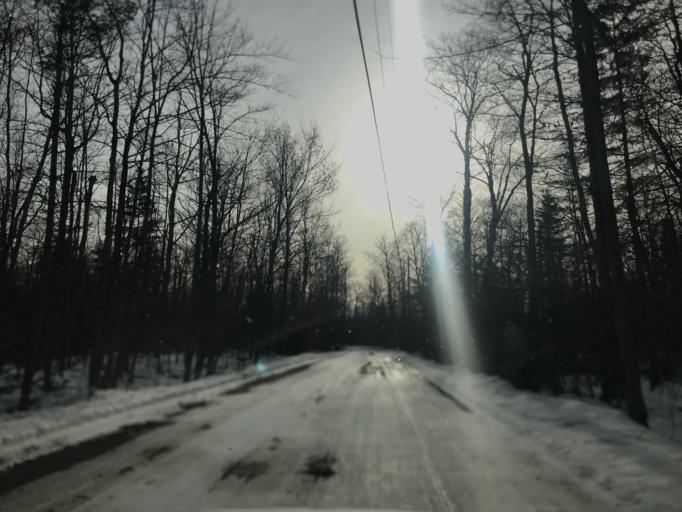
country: US
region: Wisconsin
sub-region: Door County
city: Sturgeon Bay
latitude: 45.1460
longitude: -87.0537
